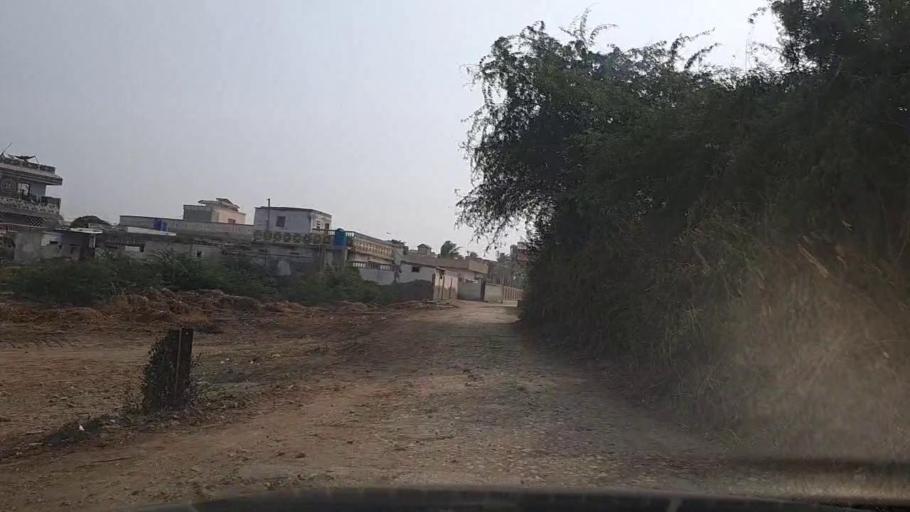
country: PK
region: Sindh
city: Thatta
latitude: 24.5560
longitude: 67.8375
